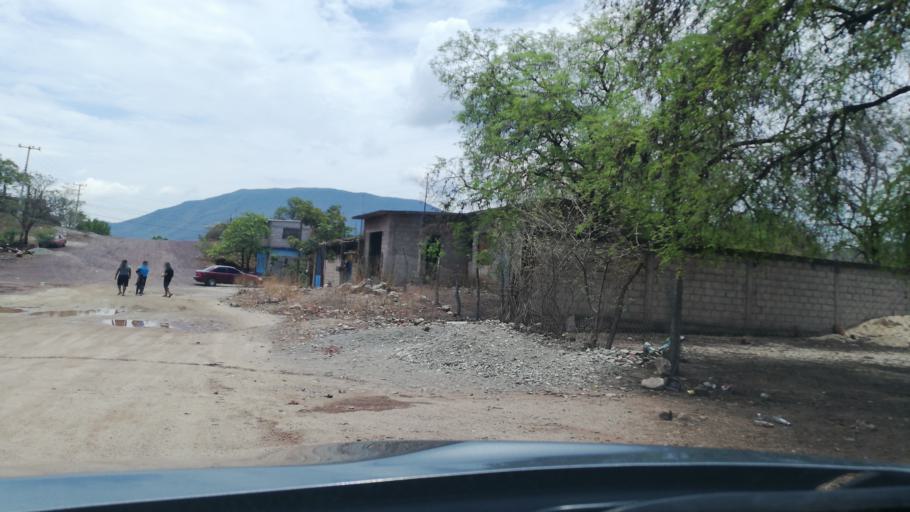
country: MX
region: Oaxaca
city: Santa Maria Jalapa del Marques
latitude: 16.4395
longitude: -95.4377
